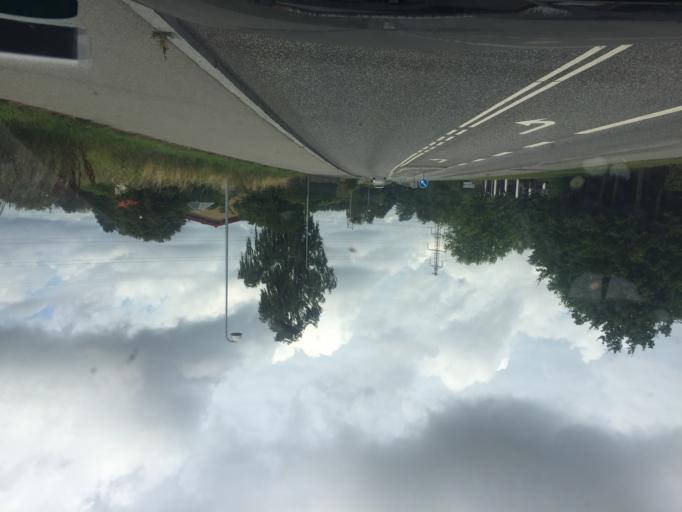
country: DK
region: Capital Region
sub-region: Allerod Kommune
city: Lillerod
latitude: 55.8891
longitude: 12.3543
